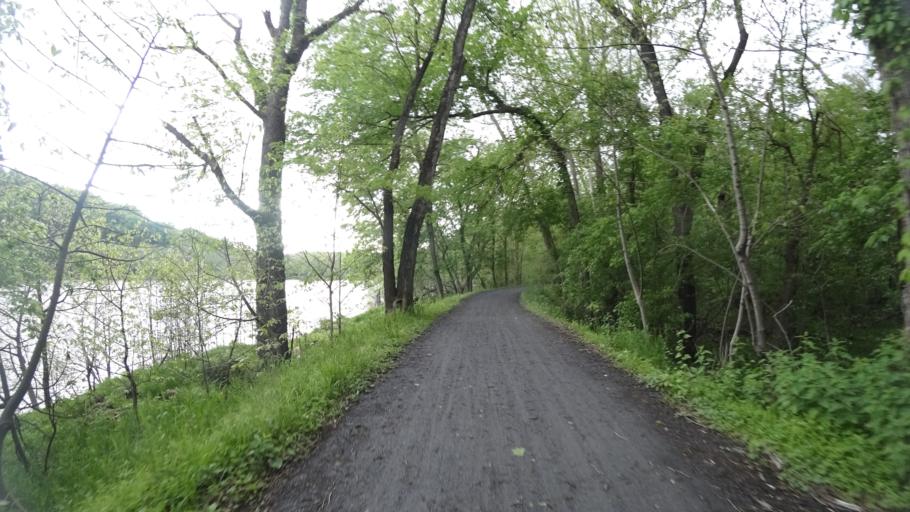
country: US
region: West Virginia
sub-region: Jefferson County
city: Bolivar
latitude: 39.3361
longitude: -77.7527
